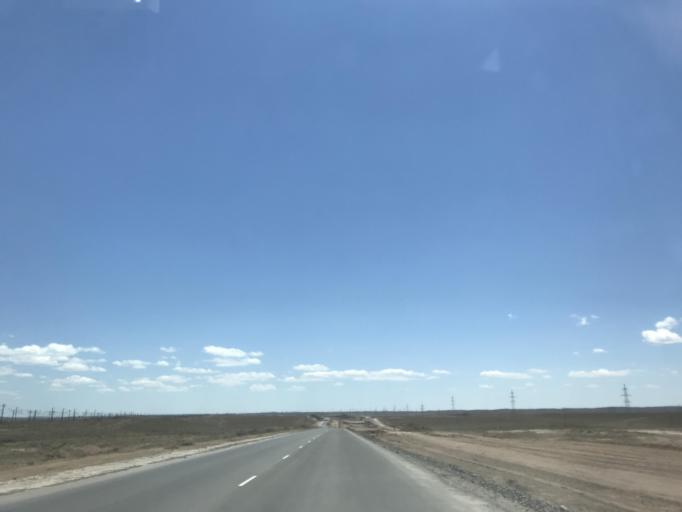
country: KZ
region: Almaty Oblysy
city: Ulken
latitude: 45.2594
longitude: 73.8023
